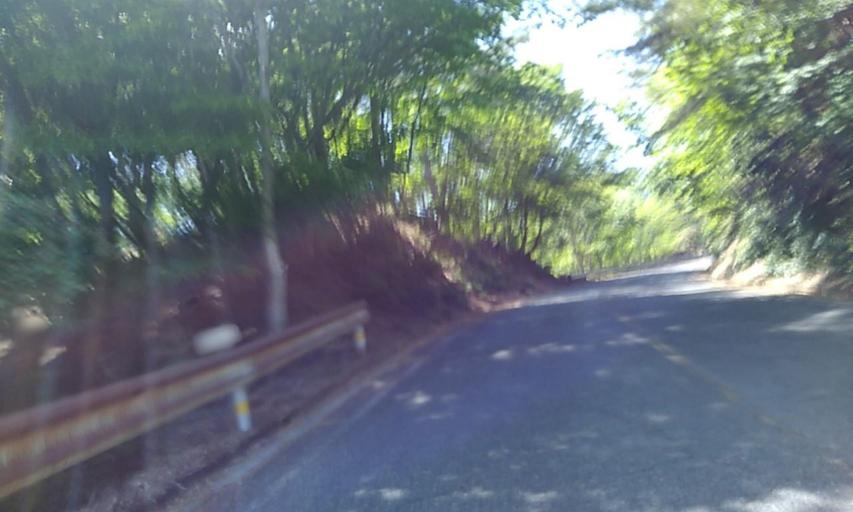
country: JP
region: Fukui
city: Obama
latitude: 35.5497
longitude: 135.7424
